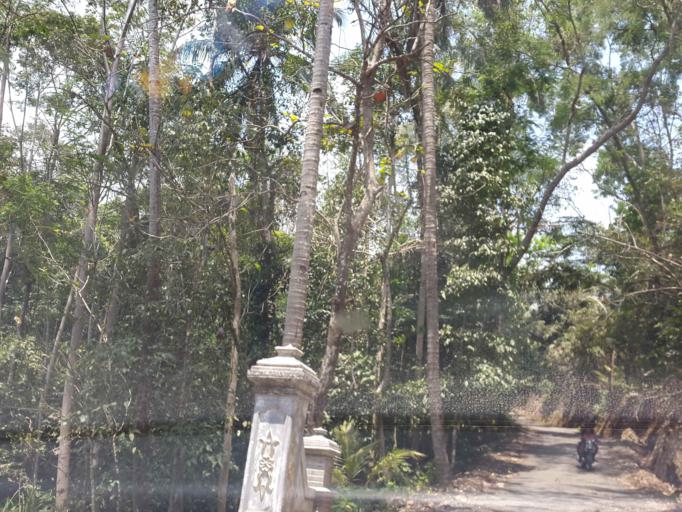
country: ID
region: East Java
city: Sudimoro
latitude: -8.2478
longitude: 111.2170
